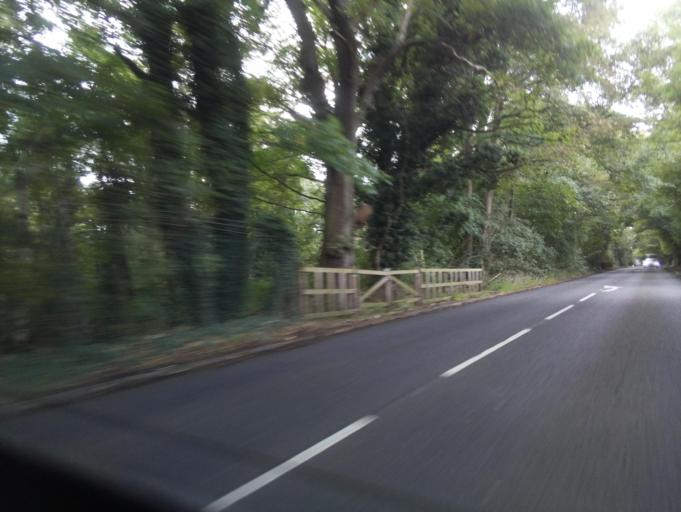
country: GB
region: England
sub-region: Staffordshire
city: Newcastle under Lyme
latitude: 52.9714
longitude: -2.2095
